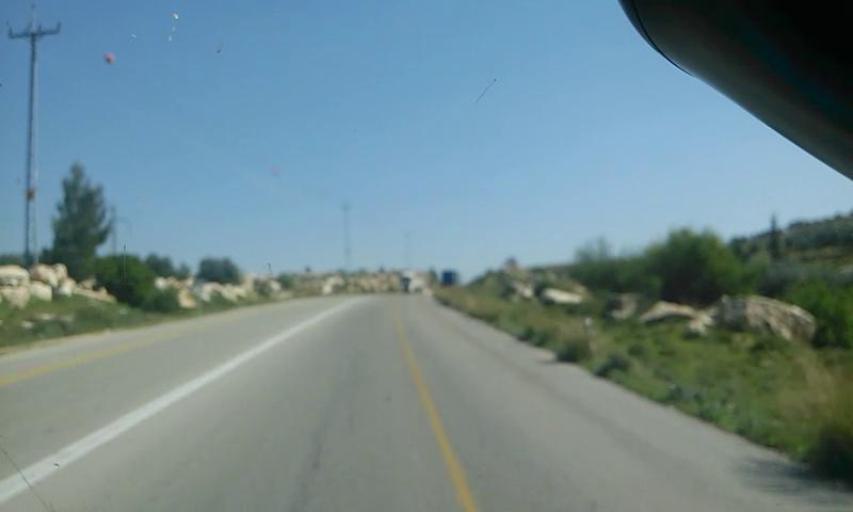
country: PS
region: West Bank
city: Tarqumya
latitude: 31.5613
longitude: 35.0027
